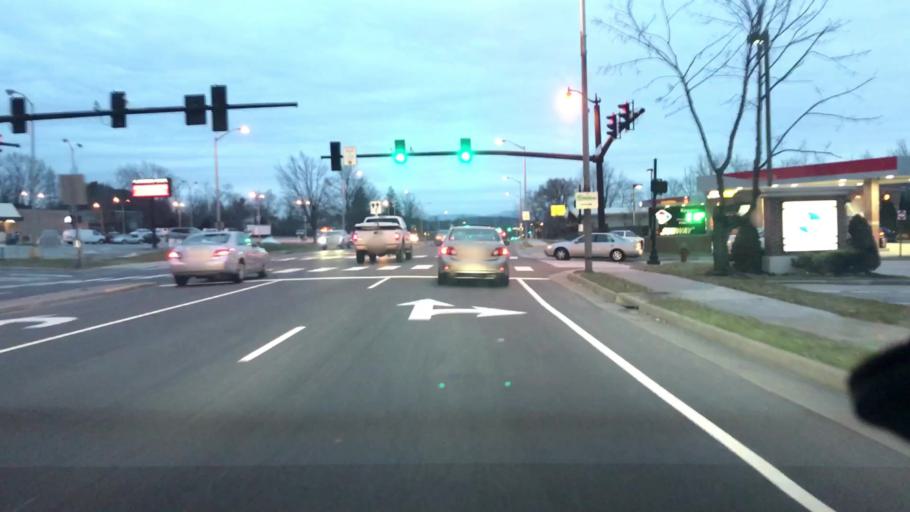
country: US
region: Virginia
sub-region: Montgomery County
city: Blacksburg
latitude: 37.2166
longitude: -80.4012
